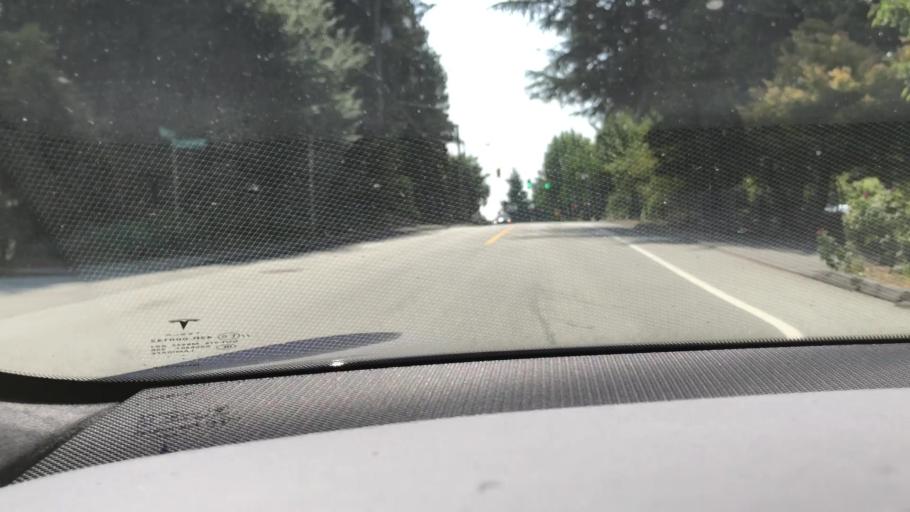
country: CA
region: British Columbia
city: Burnaby
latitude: 49.2292
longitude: -122.9627
